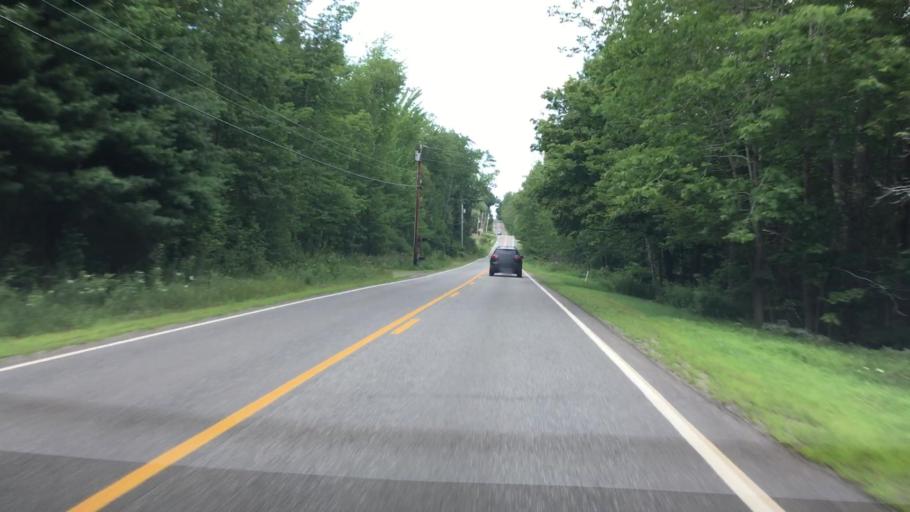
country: US
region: Maine
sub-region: Waldo County
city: Lincolnville
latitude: 44.3542
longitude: -69.0519
